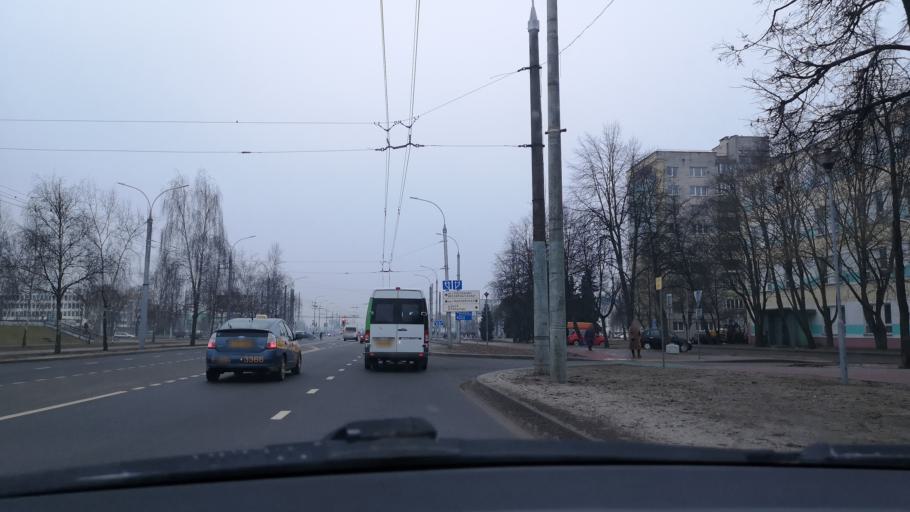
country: BY
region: Brest
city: Brest
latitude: 52.1011
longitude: 23.7630
